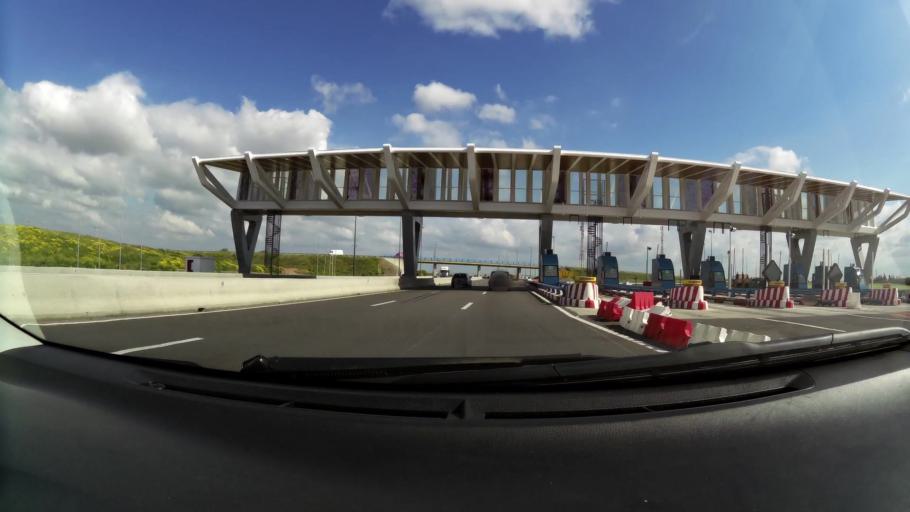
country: MA
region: Chaouia-Ouardigha
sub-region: Settat Province
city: Berrechid
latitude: 33.3183
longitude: -7.6026
